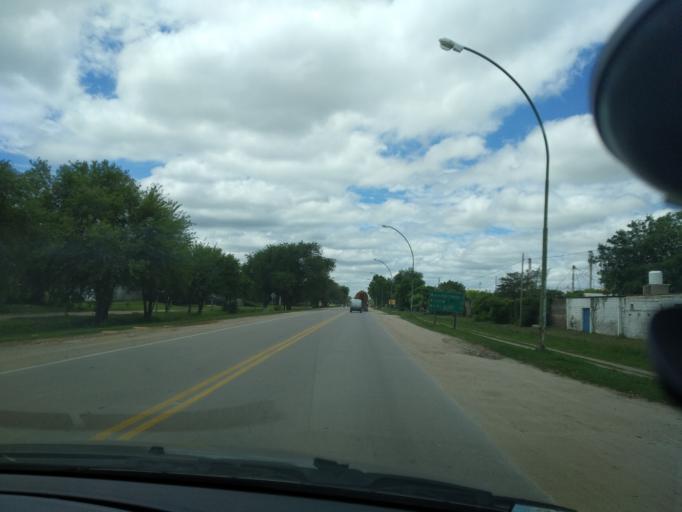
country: AR
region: Cordoba
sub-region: Departamento de Rio Segundo
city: Rio Segundo
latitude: -31.6462
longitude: -63.9037
